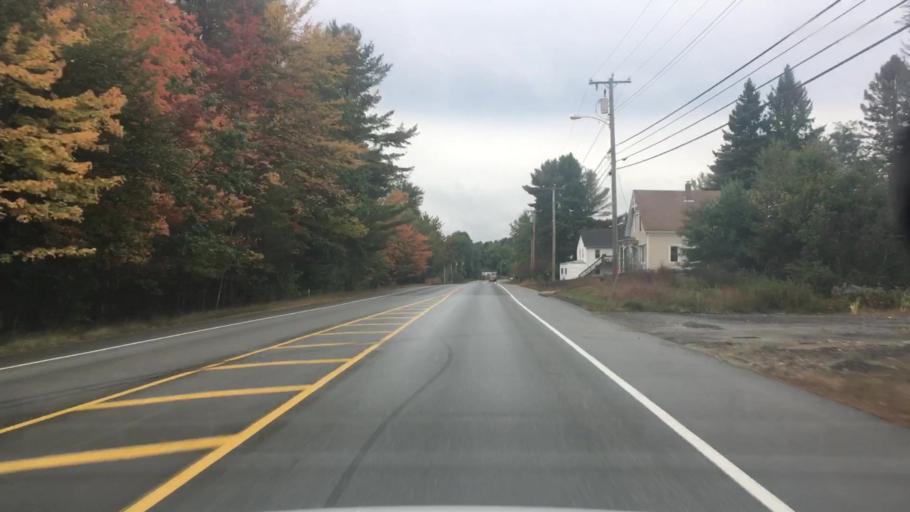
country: US
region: Maine
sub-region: Kennebec County
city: Augusta
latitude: 44.3758
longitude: -69.7974
